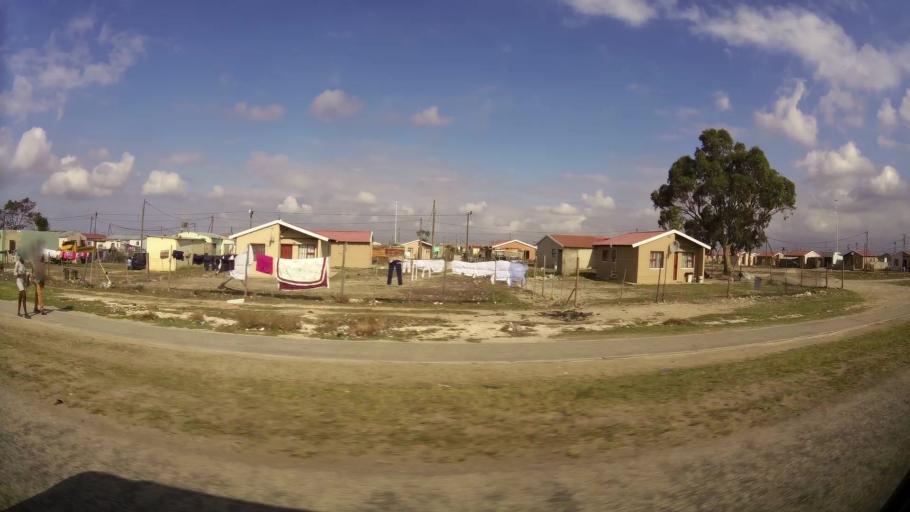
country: ZA
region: Eastern Cape
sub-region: Nelson Mandela Bay Metropolitan Municipality
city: Port Elizabeth
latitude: -33.7706
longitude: 25.5838
